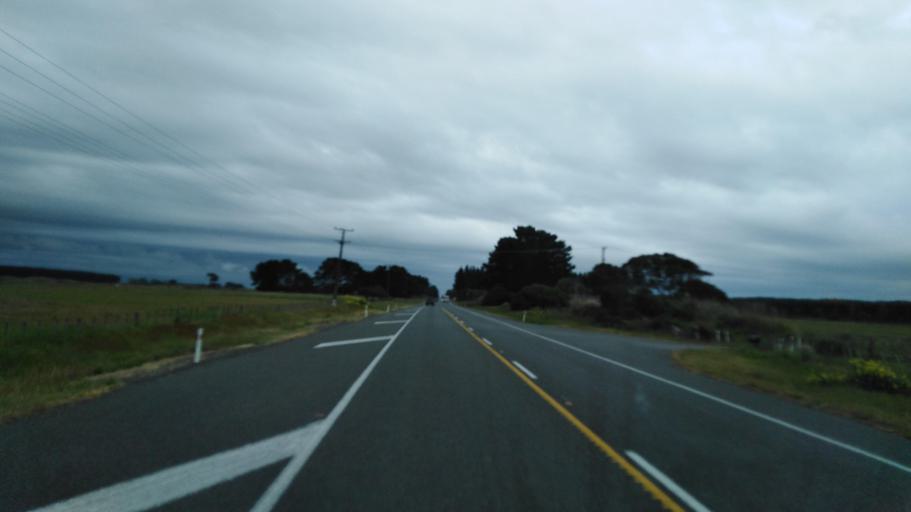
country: NZ
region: Manawatu-Wanganui
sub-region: Horowhenua District
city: Foxton
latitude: -40.4060
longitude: 175.3103
